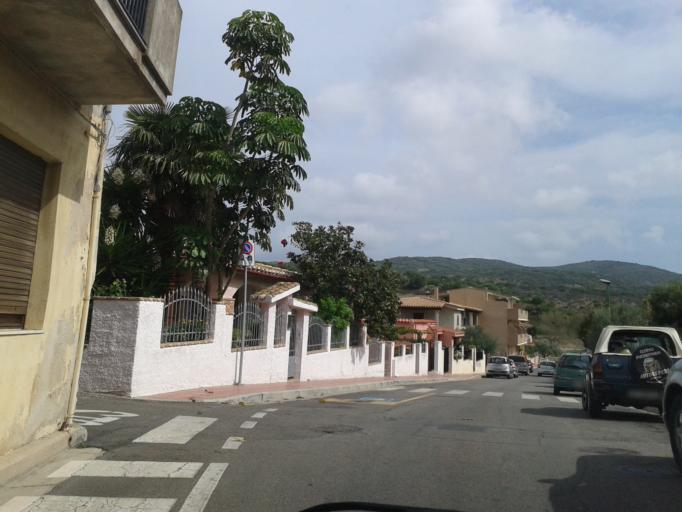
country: IT
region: Sardinia
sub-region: Provincia di Cagliari
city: Villasimius
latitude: 39.1441
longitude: 9.5234
